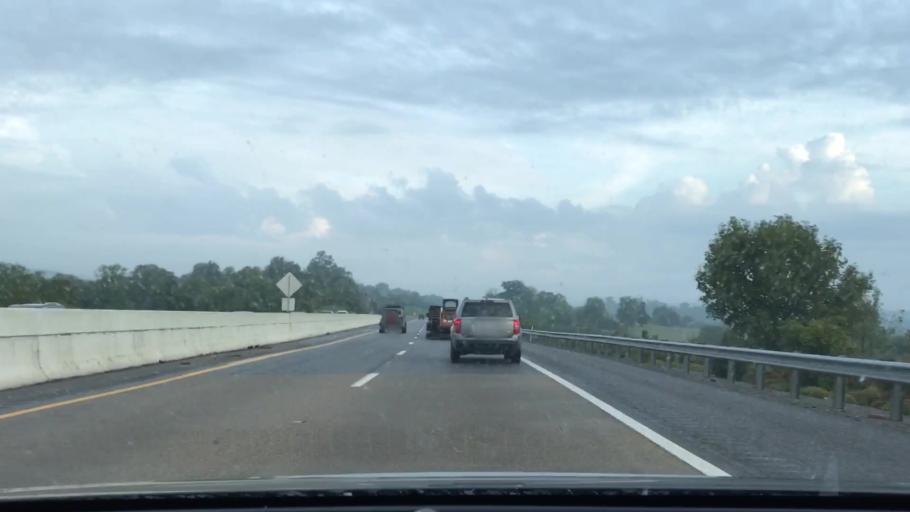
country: US
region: Tennessee
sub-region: Sumner County
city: Shackle Island
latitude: 36.3353
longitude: -86.5485
